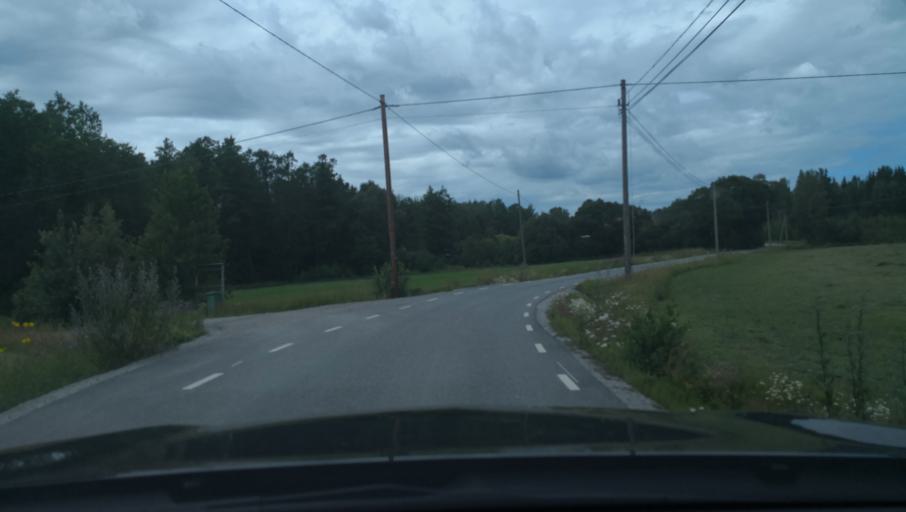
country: SE
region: Vaestmanland
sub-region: Hallstahammars Kommun
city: Hallstahammar
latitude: 59.6178
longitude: 16.1411
